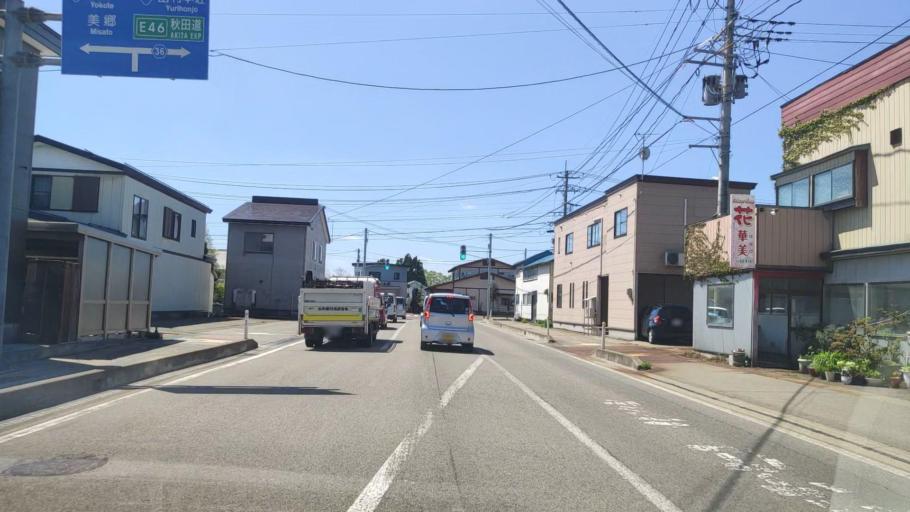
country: JP
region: Akita
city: Omagari
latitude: 39.4515
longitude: 140.4729
